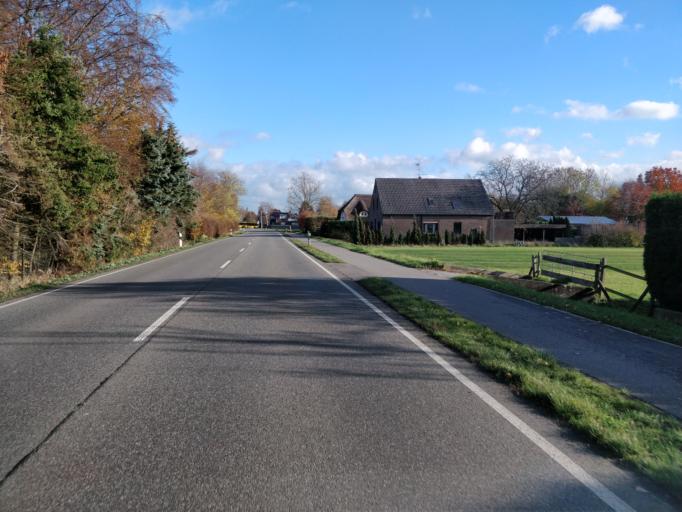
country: DE
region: North Rhine-Westphalia
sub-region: Regierungsbezirk Dusseldorf
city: Emmerich
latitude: 51.8274
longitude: 6.2962
